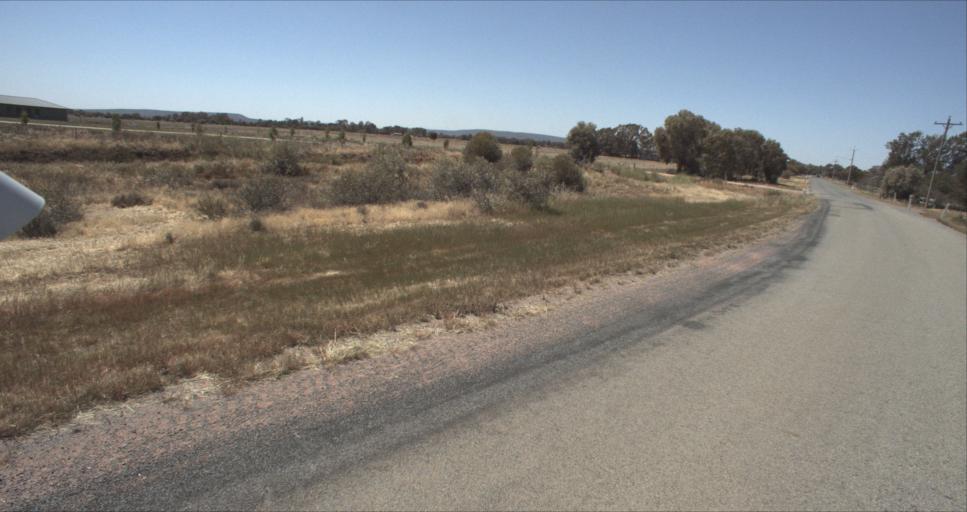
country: AU
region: New South Wales
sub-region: Leeton
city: Leeton
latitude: -34.5273
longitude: 146.3936
